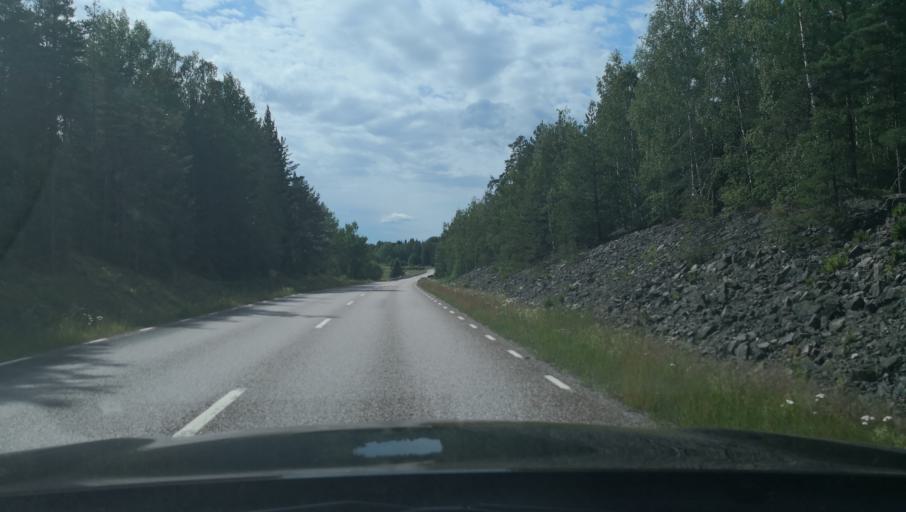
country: SE
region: Dalarna
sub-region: Avesta Kommun
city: Avesta
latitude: 59.9652
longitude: 16.1897
